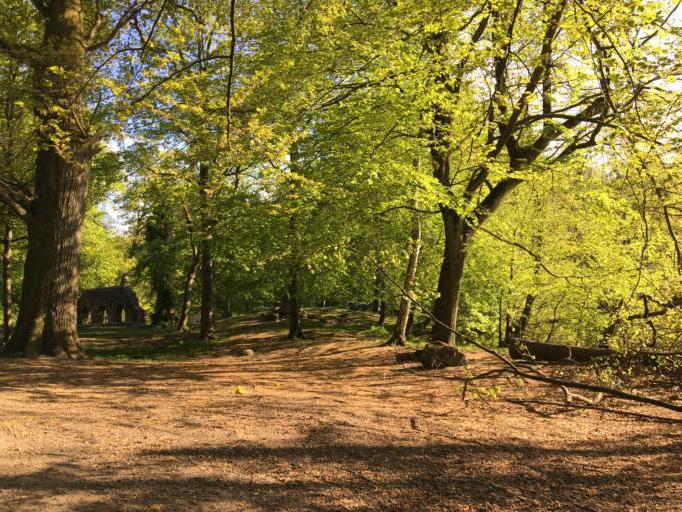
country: DK
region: Capital Region
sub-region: Hillerod Kommune
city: Hillerod
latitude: 55.9237
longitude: 12.3208
